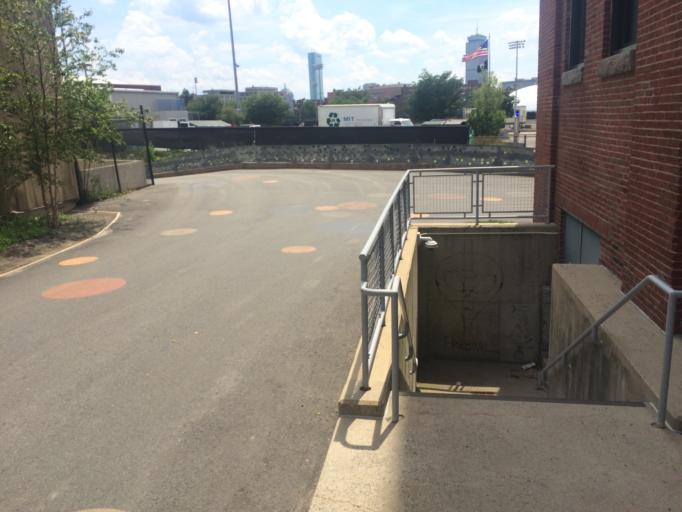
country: US
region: Massachusetts
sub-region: Middlesex County
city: Cambridge
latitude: 42.3587
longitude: -71.0995
